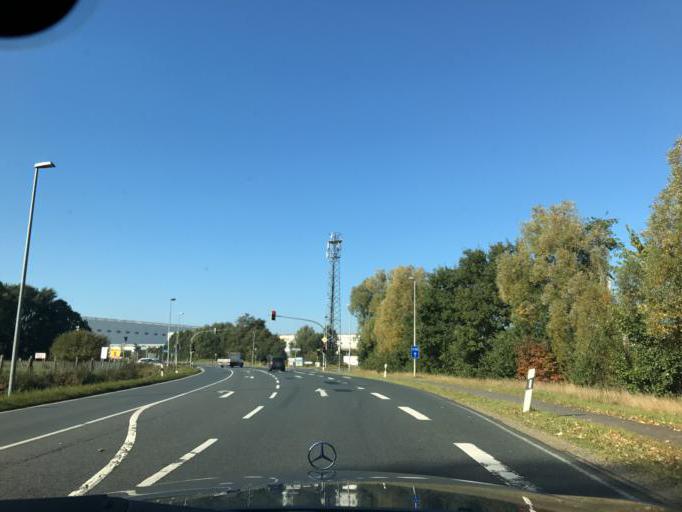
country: DE
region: Lower Saxony
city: Papenburg
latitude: 53.0895
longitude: 7.3723
